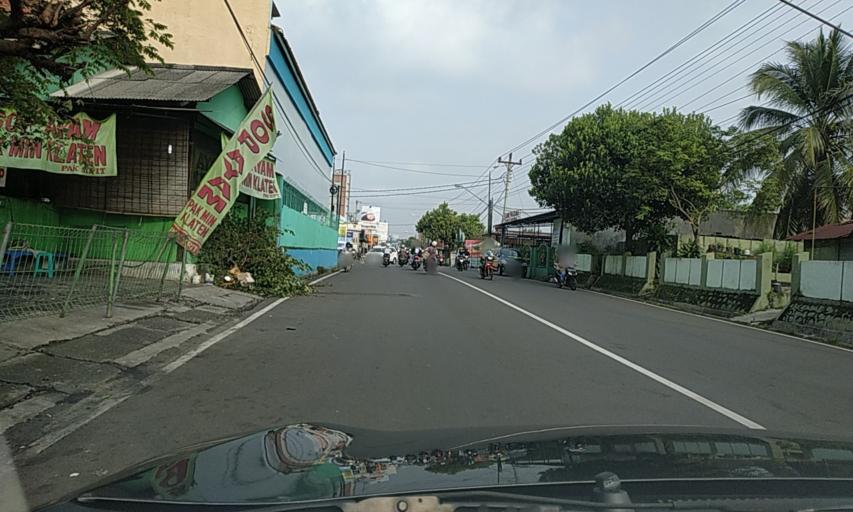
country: ID
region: Central Java
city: Purwokerto
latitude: -7.4171
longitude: 109.2477
